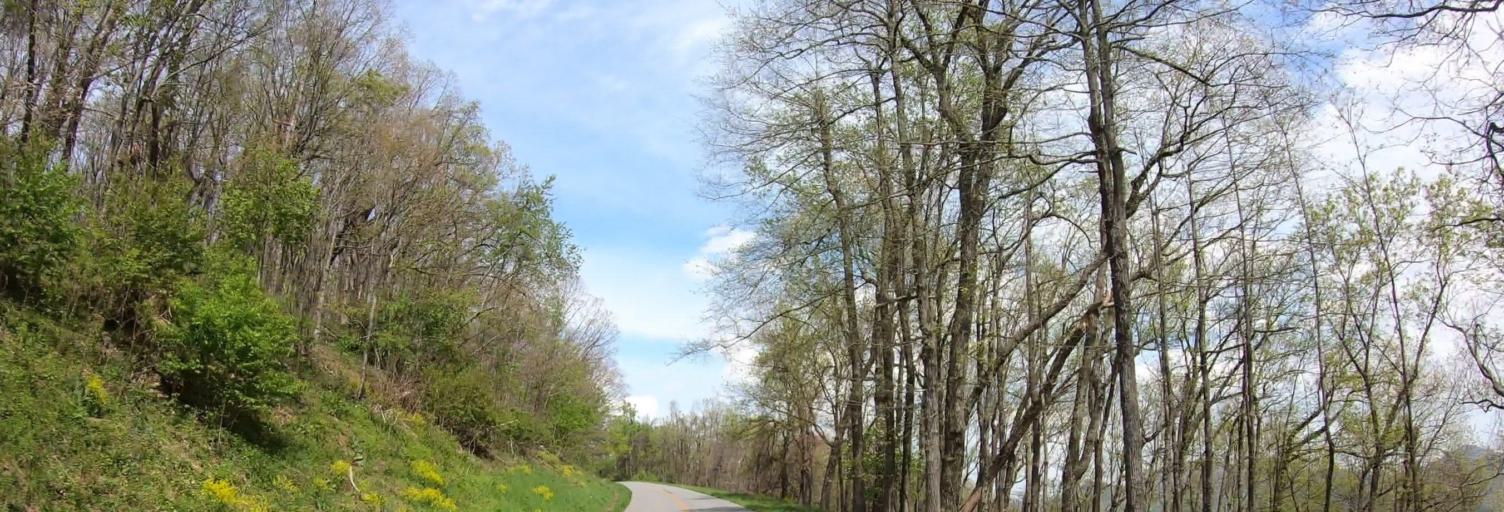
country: US
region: Virginia
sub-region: Botetourt County
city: Buchanan
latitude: 37.4795
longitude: -79.6812
